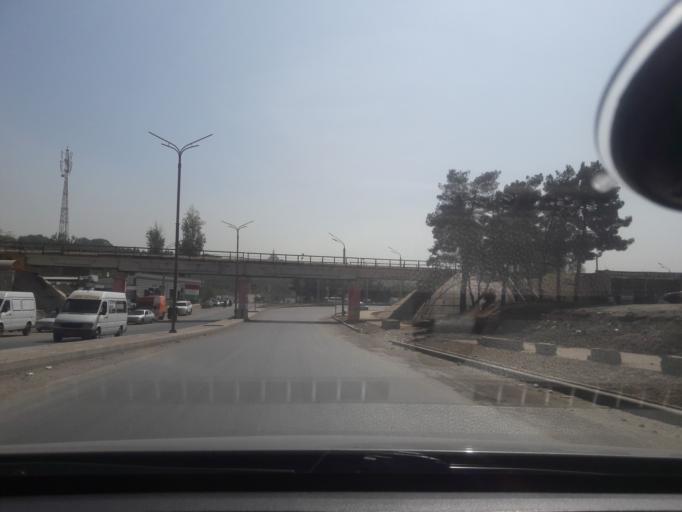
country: TJ
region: Dushanbe
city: Dushanbe
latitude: 38.6034
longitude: 68.7740
